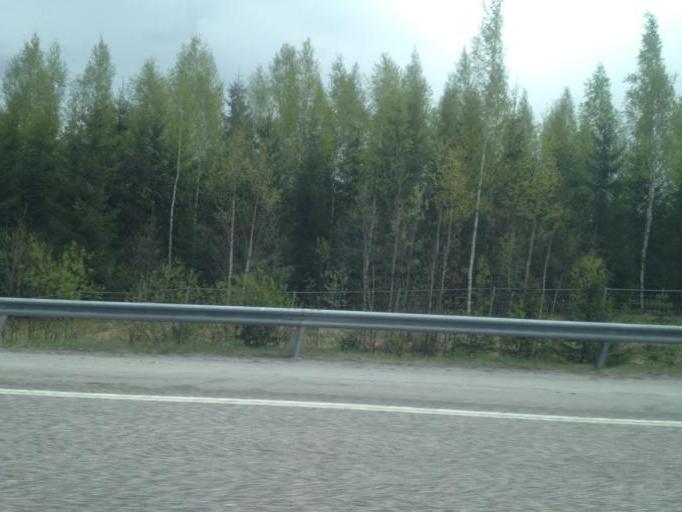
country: FI
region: Uusimaa
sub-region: Helsinki
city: Hyvinge
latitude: 60.6063
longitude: 24.8020
